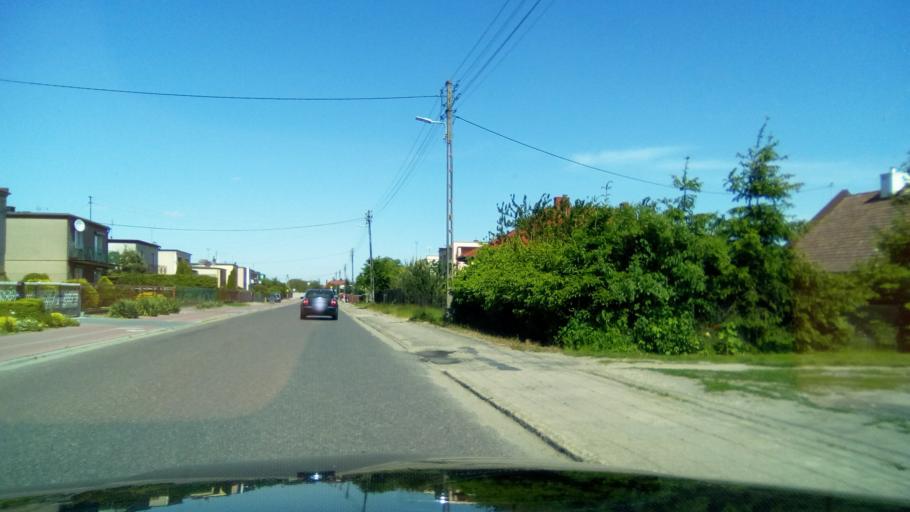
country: PL
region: Greater Poland Voivodeship
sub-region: Powiat gnieznienski
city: Niechanowo
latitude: 52.4637
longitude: 17.6737
